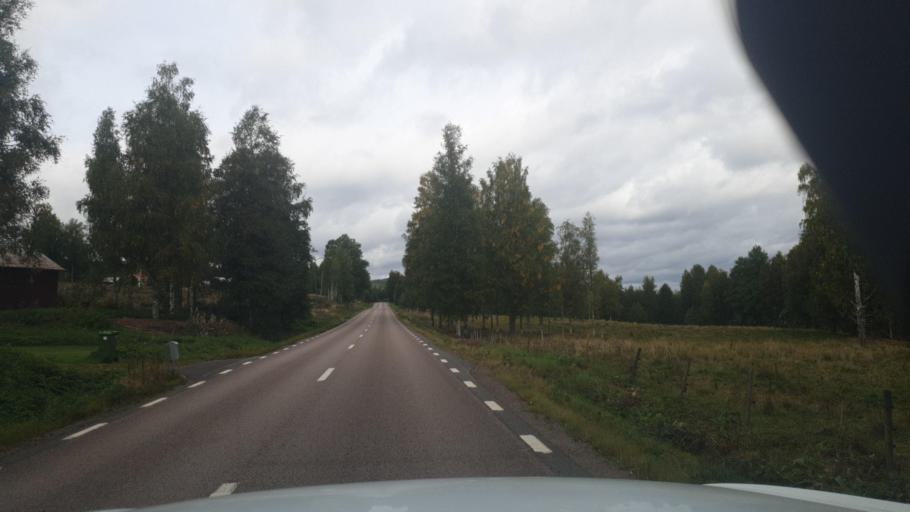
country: SE
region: Vaermland
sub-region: Sunne Kommun
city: Sunne
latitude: 59.8989
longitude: 12.9141
